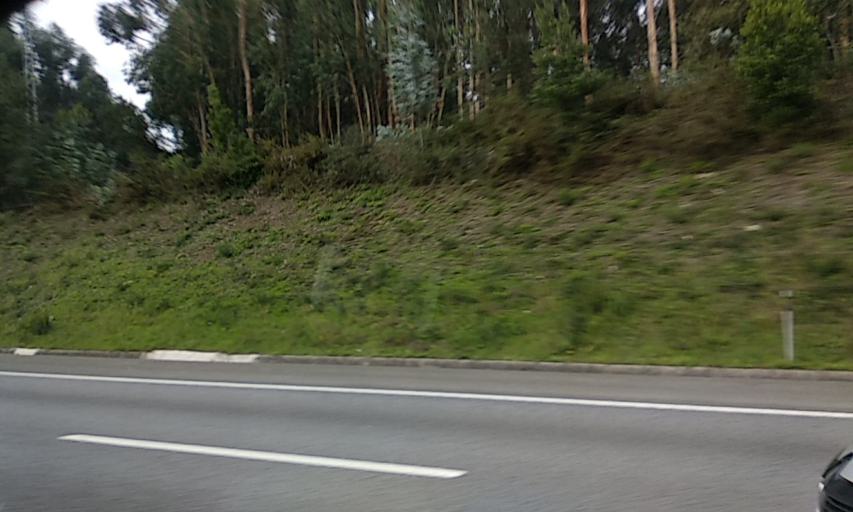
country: PT
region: Porto
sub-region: Maia
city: Aguas Santas
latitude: 41.2156
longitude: -8.5759
